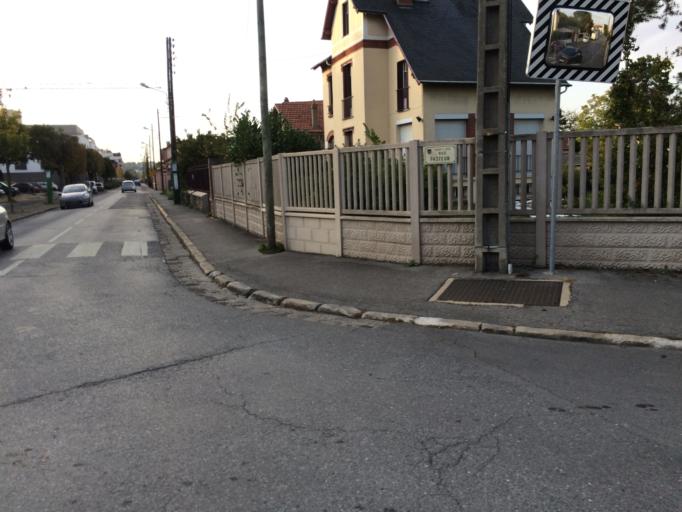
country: FR
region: Ile-de-France
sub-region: Departement de l'Essonne
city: Vigneux-sur-Seine
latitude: 48.7048
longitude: 2.4272
